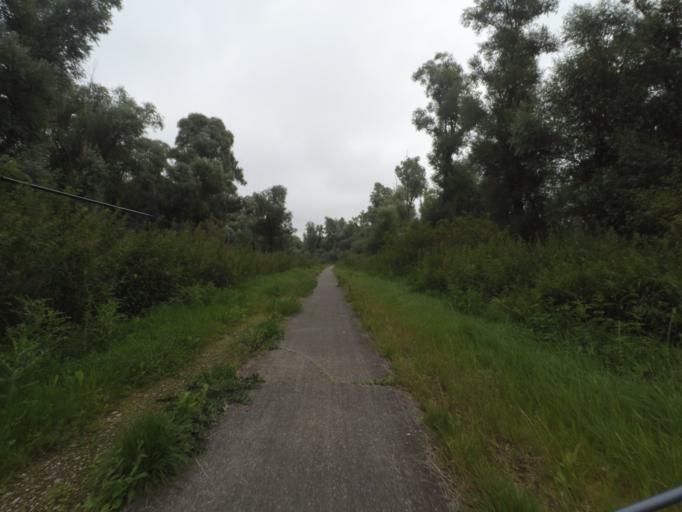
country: NL
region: Flevoland
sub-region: Gemeente Lelystad
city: Lelystad
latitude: 52.4390
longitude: 5.4210
